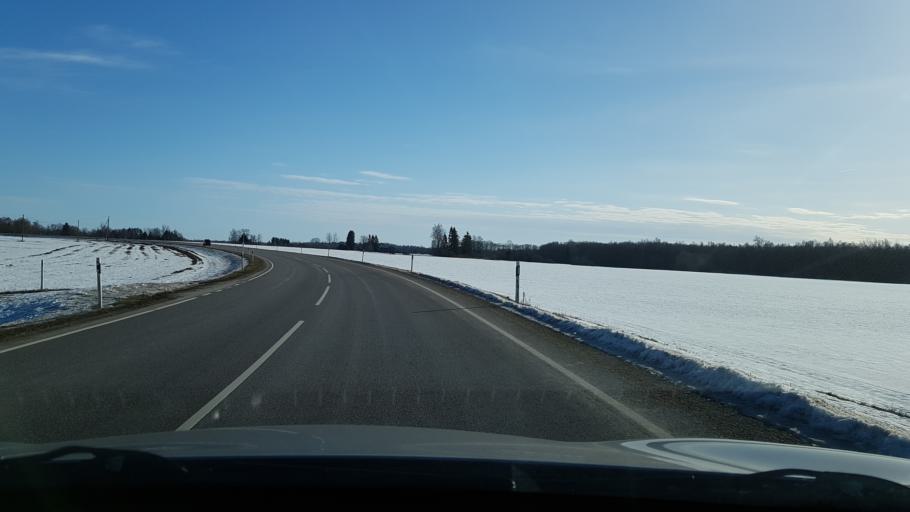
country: EE
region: Jogevamaa
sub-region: Poltsamaa linn
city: Poltsamaa
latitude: 58.6306
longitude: 25.7815
